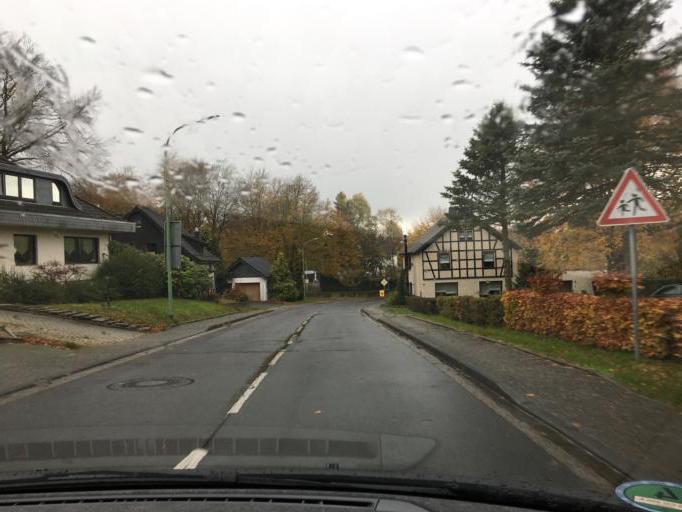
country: DE
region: North Rhine-Westphalia
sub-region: Regierungsbezirk Koln
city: Simmerath
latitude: 50.6278
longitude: 6.3522
